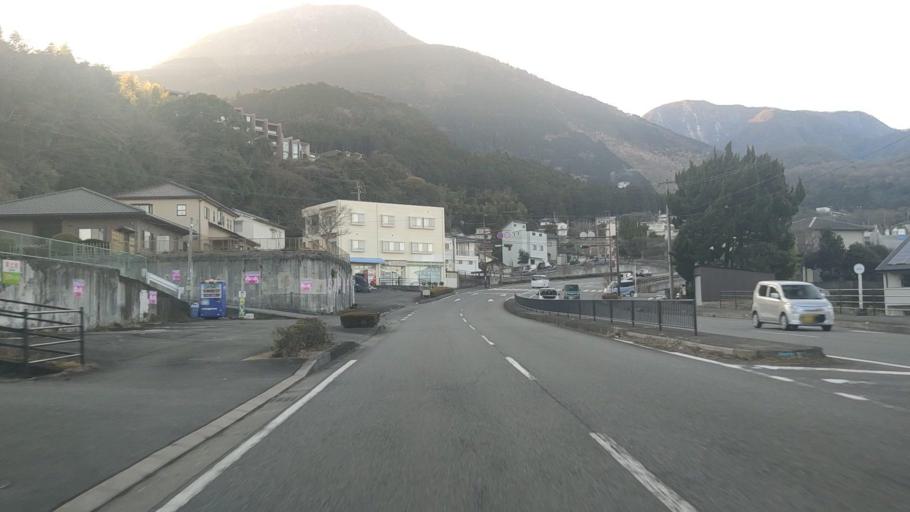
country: JP
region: Oita
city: Beppu
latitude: 33.2877
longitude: 131.4637
